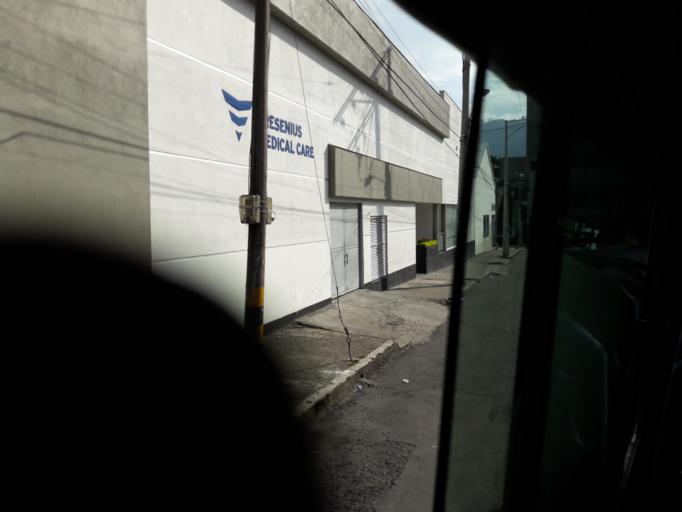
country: CO
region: Tolima
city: Ibague
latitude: 4.4367
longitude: -75.2126
